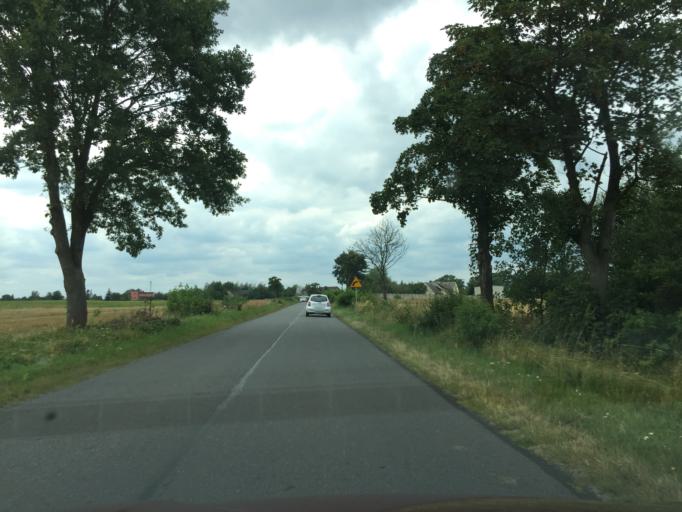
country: PL
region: Greater Poland Voivodeship
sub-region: Powiat kaliski
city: Stawiszyn
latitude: 51.9484
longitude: 18.1693
